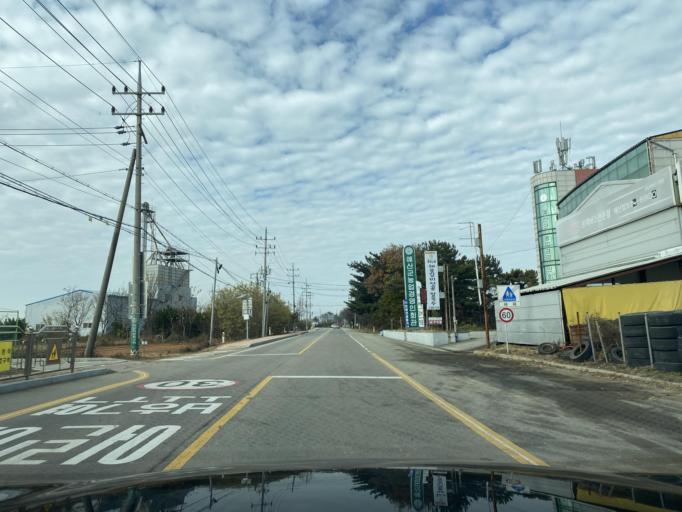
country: KR
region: Chungcheongnam-do
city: Yesan
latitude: 36.6885
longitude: 126.7933
